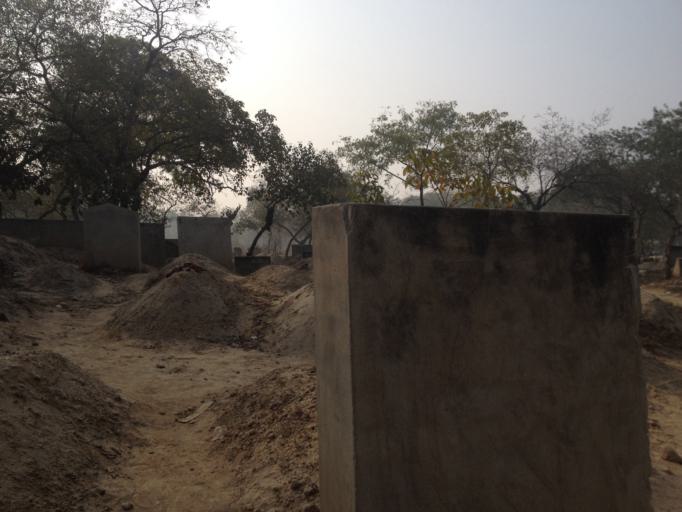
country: PK
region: Punjab
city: Lahore
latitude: 31.5789
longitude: 74.4160
